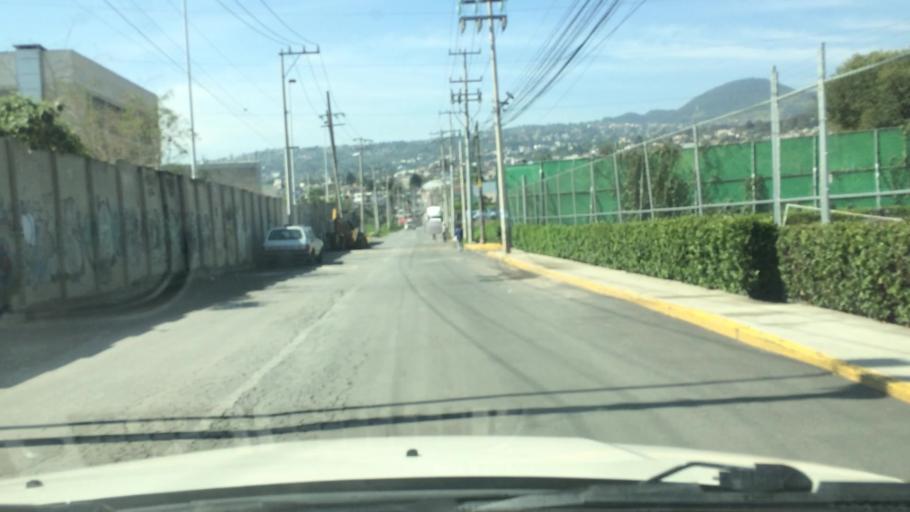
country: MX
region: Mexico City
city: Tlalpan
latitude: 19.2607
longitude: -99.1723
